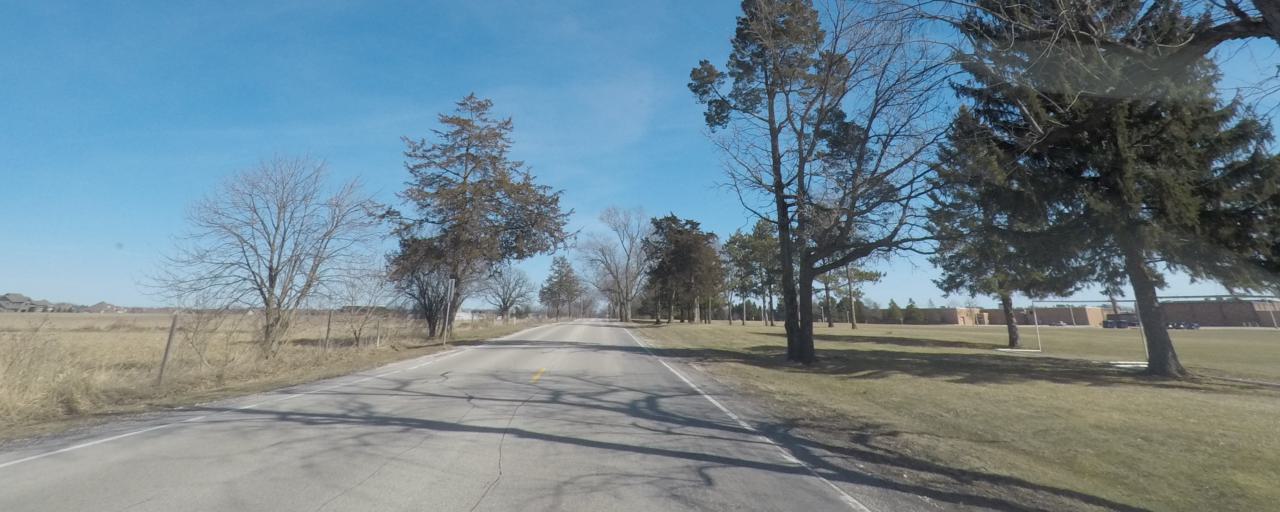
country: US
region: Wisconsin
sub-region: Waukesha County
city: Hartland
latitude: 43.1199
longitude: -88.3512
